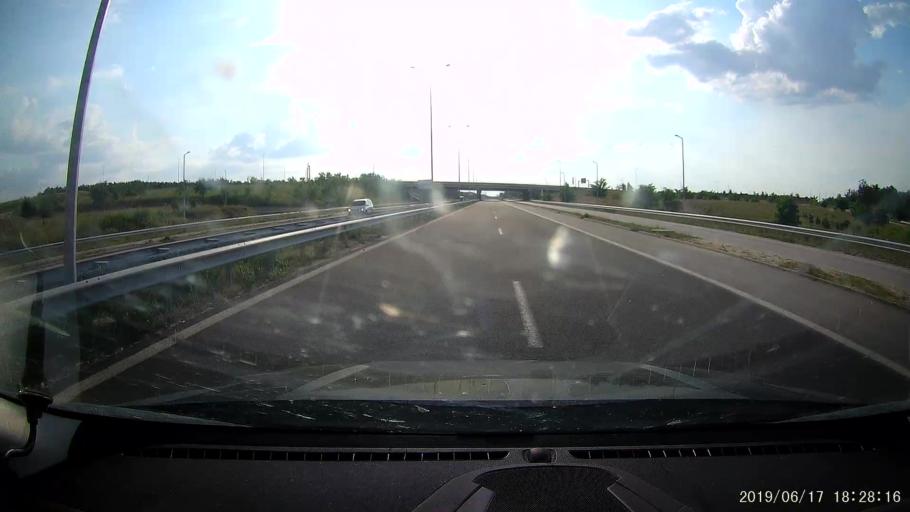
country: BG
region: Khaskovo
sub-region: Obshtina Dimitrovgrad
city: Dimitrovgrad
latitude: 42.0218
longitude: 25.5844
